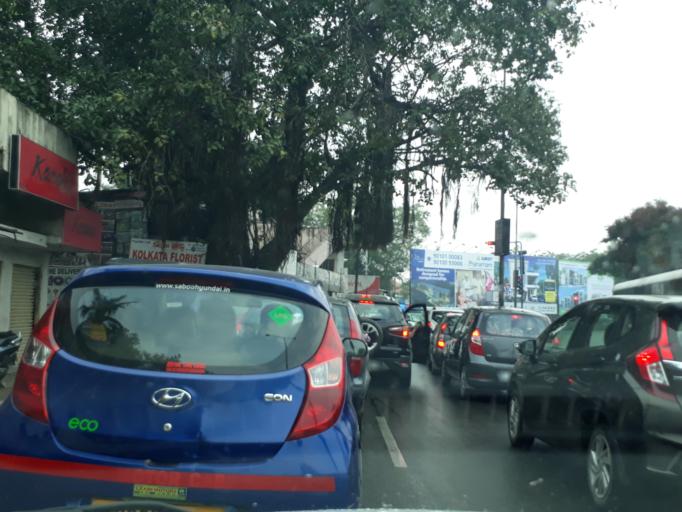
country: IN
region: Telangana
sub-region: Hyderabad
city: Malkajgiri
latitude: 17.4547
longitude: 78.4983
